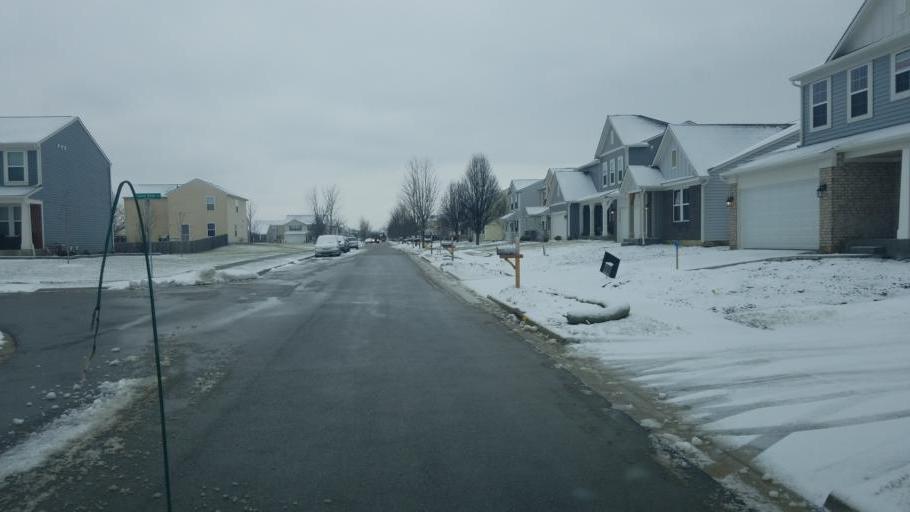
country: US
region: Ohio
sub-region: Franklin County
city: Reynoldsburg
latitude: 40.0123
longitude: -82.7974
